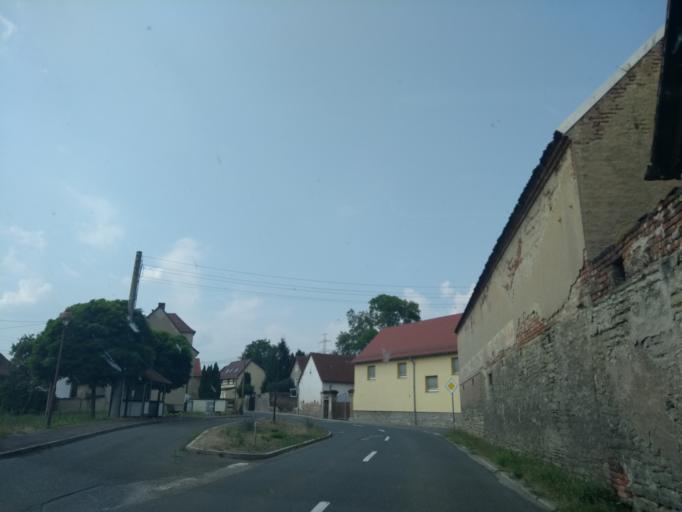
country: DE
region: Saxony-Anhalt
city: Droyssig
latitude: 51.0231
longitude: 12.0466
